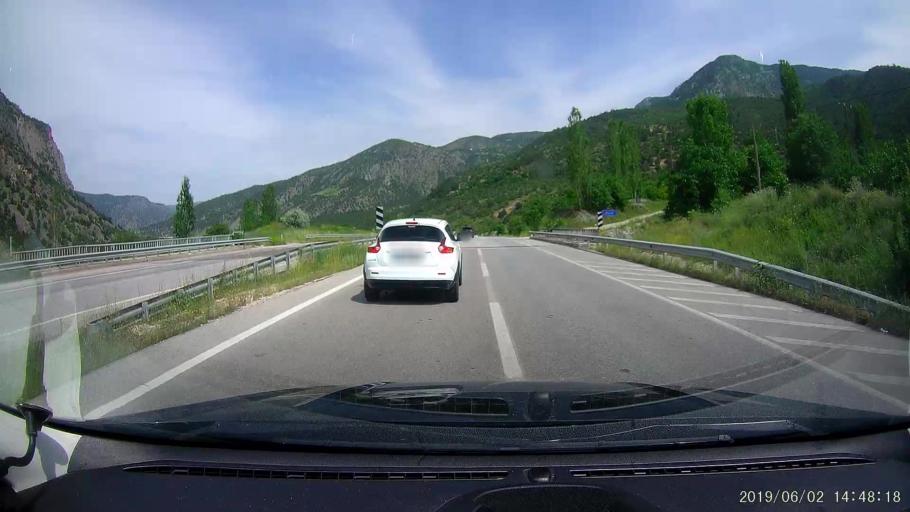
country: TR
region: Corum
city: Hacihamza
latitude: 41.0635
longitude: 34.4775
